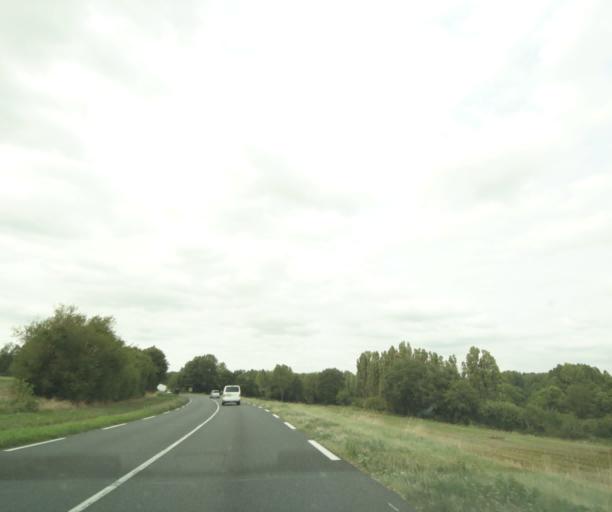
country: FR
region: Centre
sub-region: Departement de l'Indre
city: Chatillon-sur-Indre
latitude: 47.0446
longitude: 1.0953
